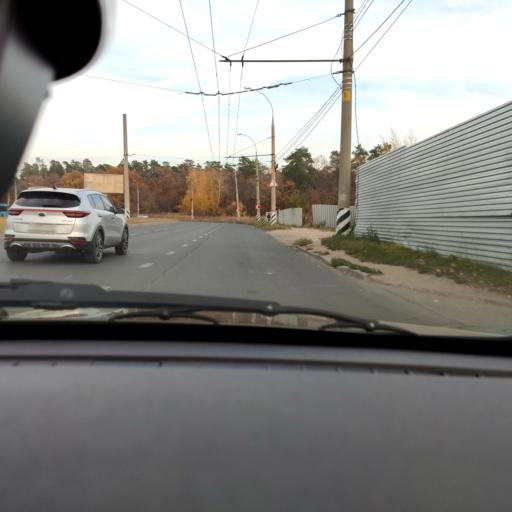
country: RU
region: Samara
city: Tol'yatti
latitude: 53.4977
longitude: 49.2940
